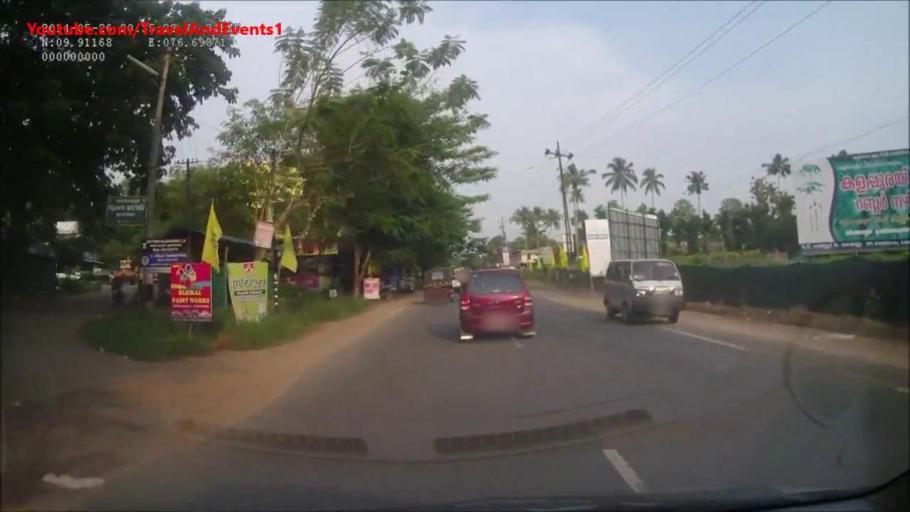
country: IN
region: Kerala
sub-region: Ernakulam
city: Muvattupula
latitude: 9.9129
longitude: 76.6966
